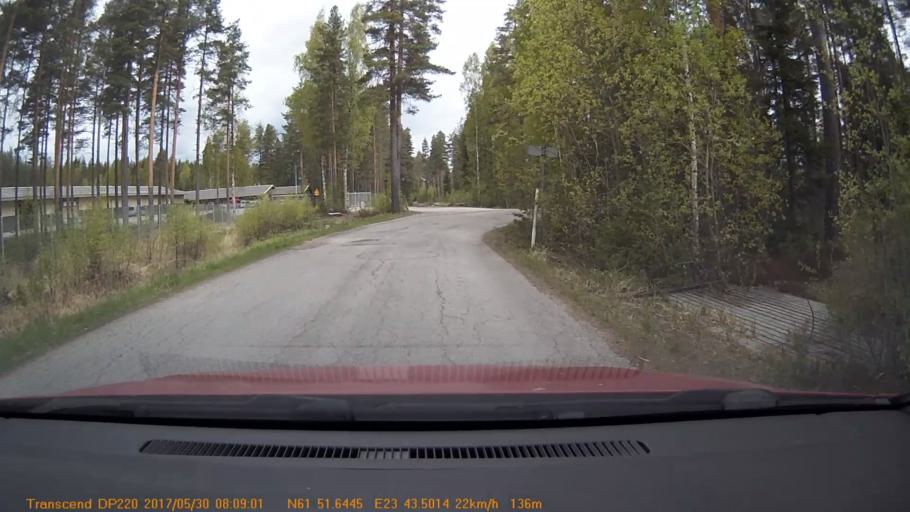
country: FI
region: Pirkanmaa
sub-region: Tampere
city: Kuru
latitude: 61.8606
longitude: 23.7250
